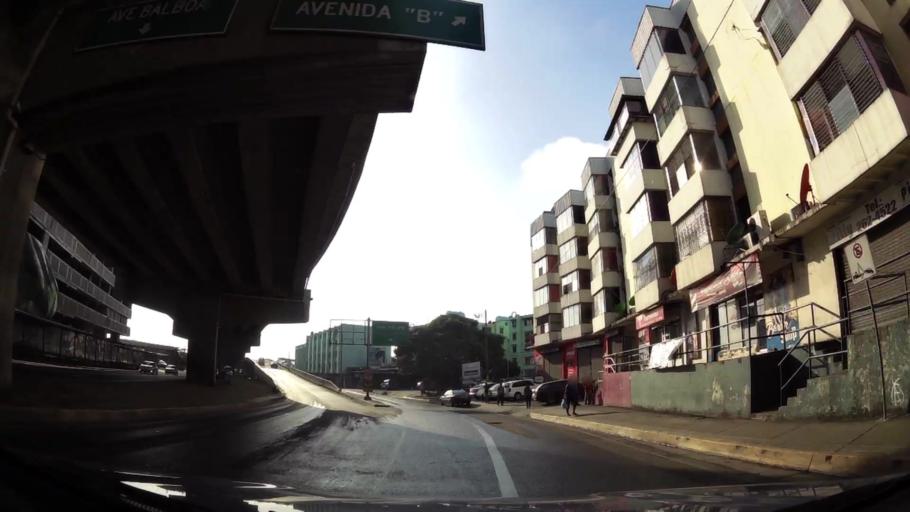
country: PA
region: Panama
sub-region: Distrito de Panama
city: Ancon
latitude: 8.9603
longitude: -79.5391
